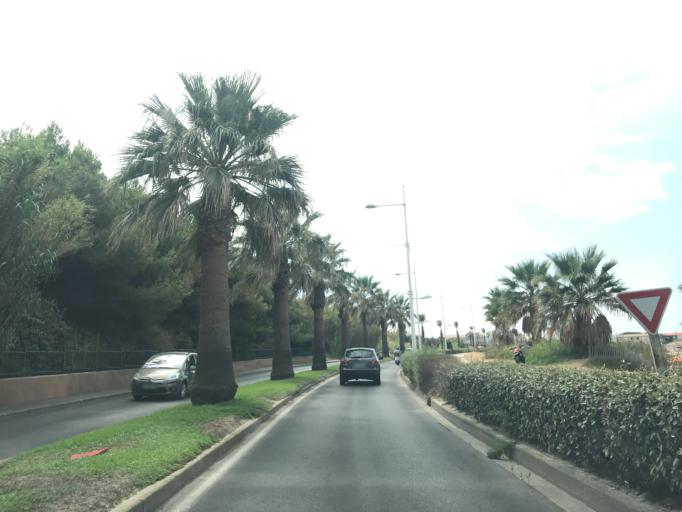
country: FR
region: Provence-Alpes-Cote d'Azur
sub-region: Departement du Var
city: Sanary-sur-Mer
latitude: 43.0956
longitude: 5.8129
